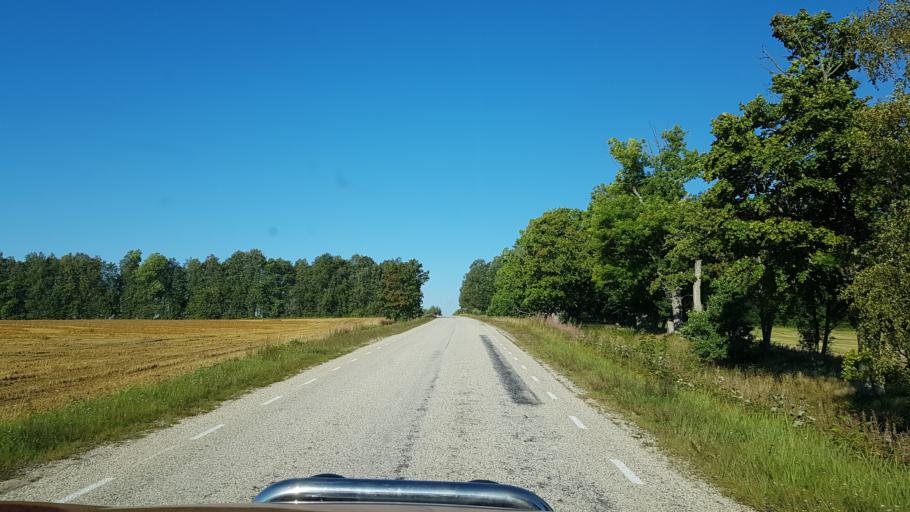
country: EE
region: Jogevamaa
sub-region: Tabivere vald
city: Tabivere
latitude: 58.6693
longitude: 26.7659
